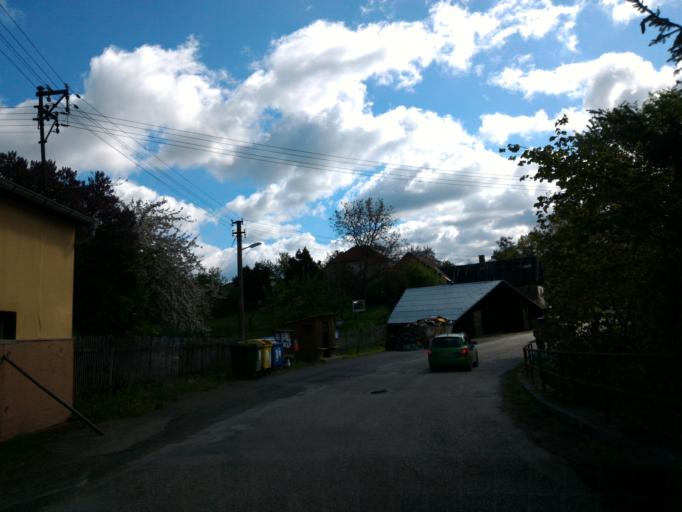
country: CZ
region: Vysocina
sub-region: Okres Pelhrimov
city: Humpolec
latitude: 49.6204
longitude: 15.3263
